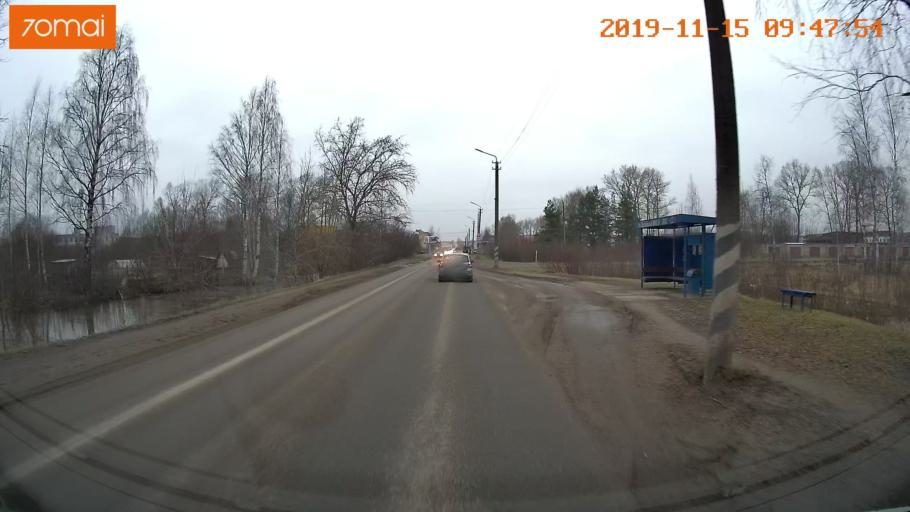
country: RU
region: Vologda
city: Sheksna
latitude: 59.2194
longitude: 38.5113
